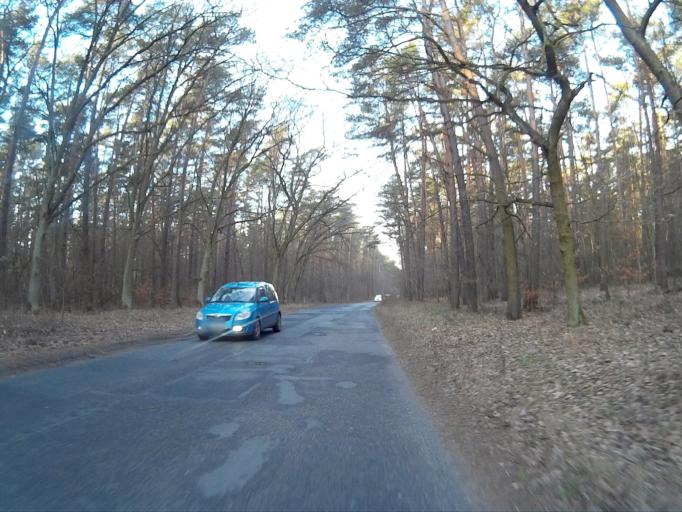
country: PL
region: Kujawsko-Pomorskie
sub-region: Powiat bydgoski
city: Osielsko
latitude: 53.1603
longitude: 18.0681
